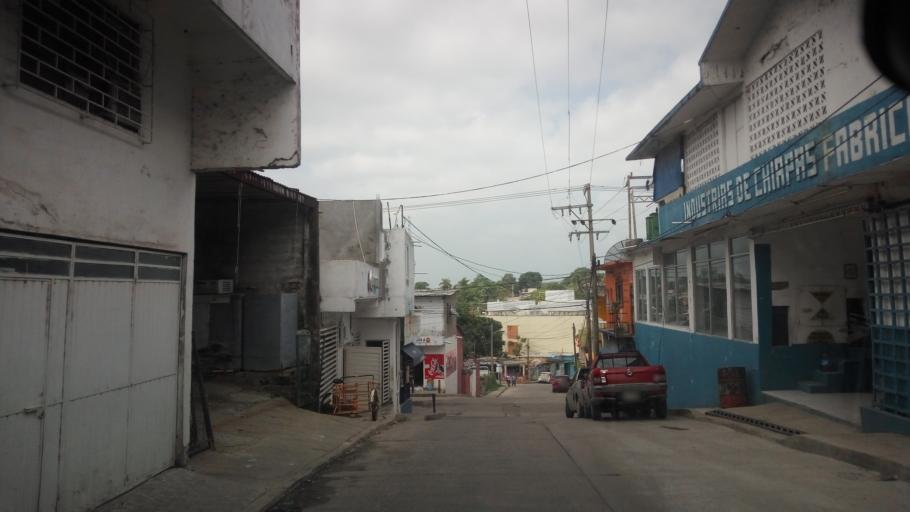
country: MX
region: Chiapas
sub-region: Reforma
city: El Carmen (El Limon)
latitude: 17.8669
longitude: -93.1482
